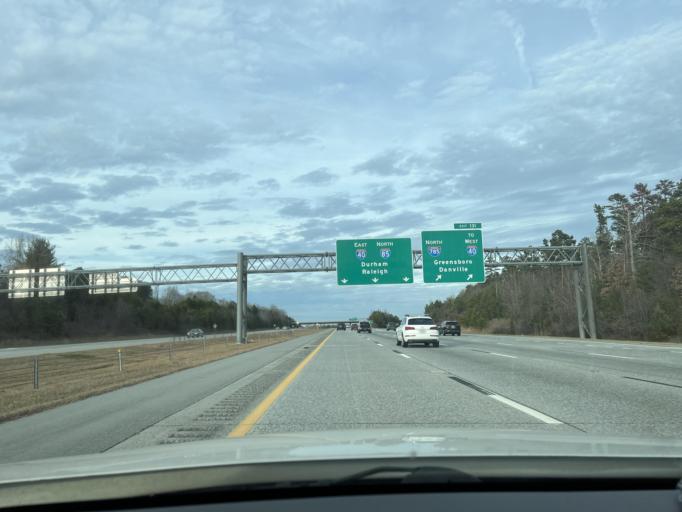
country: US
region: North Carolina
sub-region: Guilford County
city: Forest Oaks
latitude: 36.0482
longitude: -79.6871
